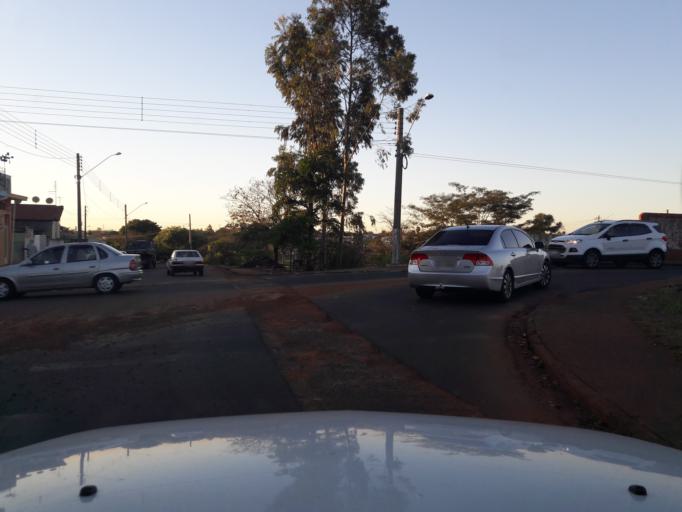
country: BR
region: Sao Paulo
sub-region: Moji-Guacu
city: Mogi-Gaucu
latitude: -22.3449
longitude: -46.9347
